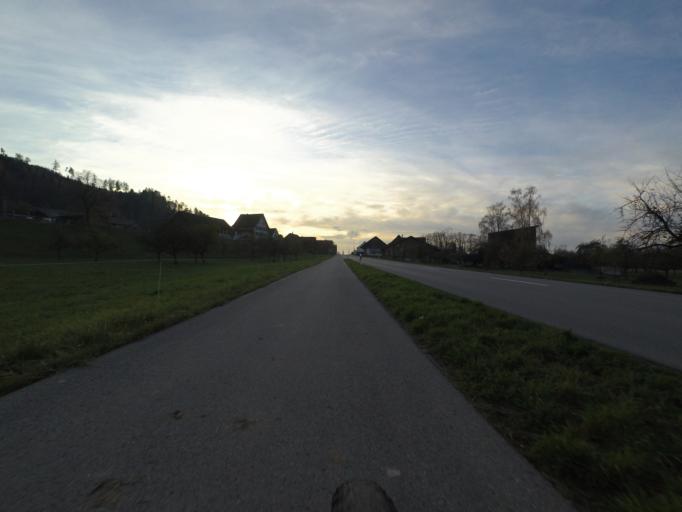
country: CH
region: Thurgau
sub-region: Frauenfeld District
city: Mullheim
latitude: 47.5788
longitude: 8.9830
